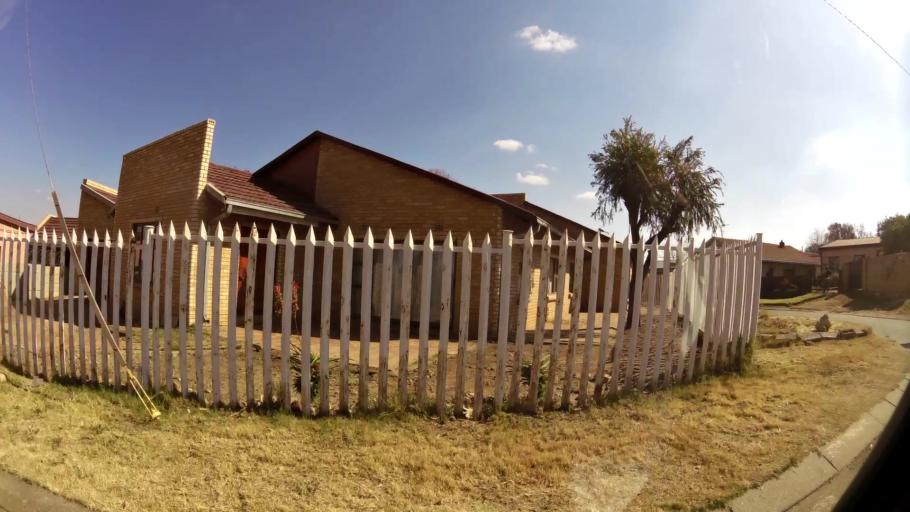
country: ZA
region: Gauteng
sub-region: City of Johannesburg Metropolitan Municipality
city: Soweto
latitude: -26.2407
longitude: 27.8950
